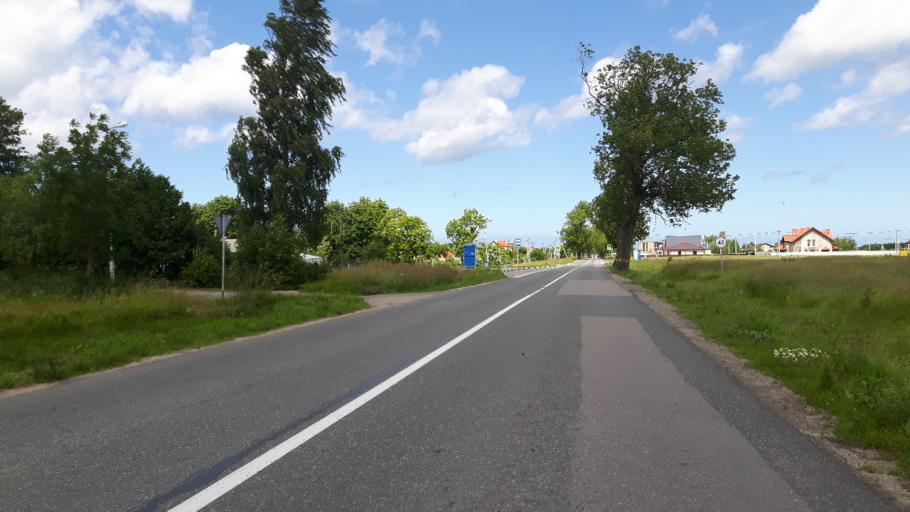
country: RU
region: Kaliningrad
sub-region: Zelenogradskiy Rayon
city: Zelenogradsk
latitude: 54.9015
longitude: 20.4030
